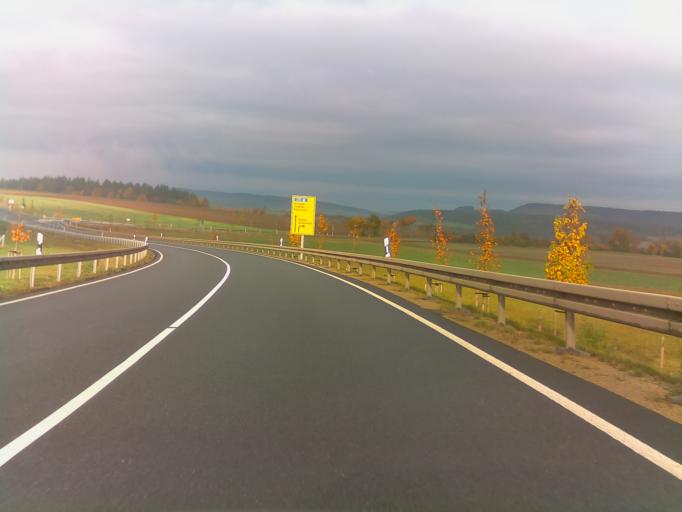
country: DE
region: Thuringia
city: Rottenbach
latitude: 50.7313
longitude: 11.2196
